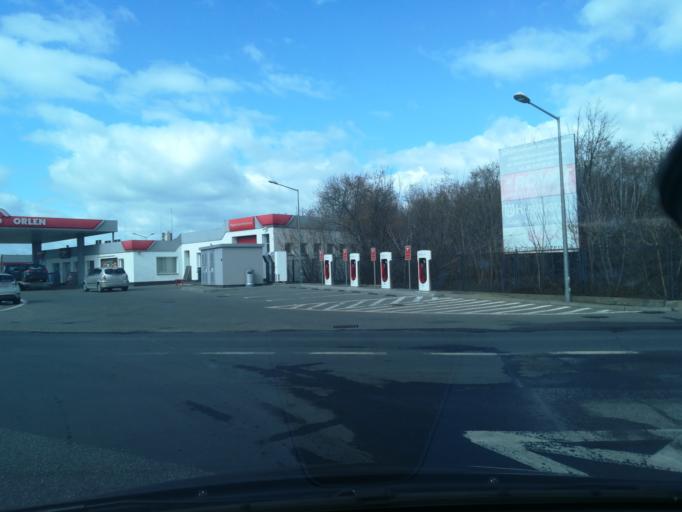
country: PL
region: Kujawsko-Pomorskie
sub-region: Powiat aleksandrowski
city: Ciechocinek
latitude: 52.8750
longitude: 18.7752
